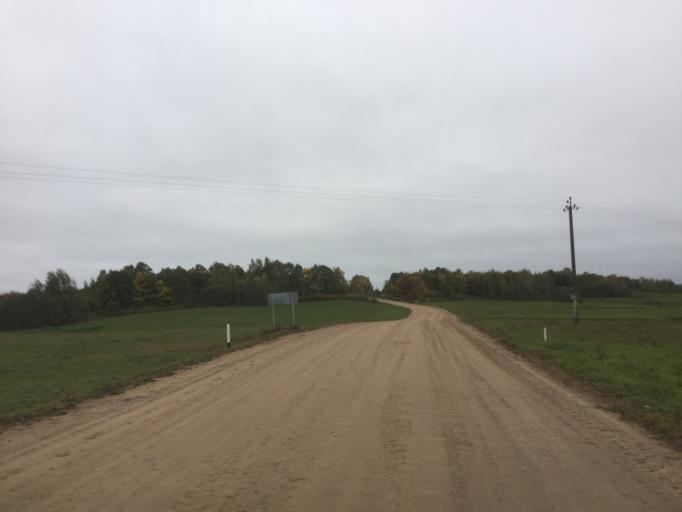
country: BY
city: Novolukoml'
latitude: 54.7163
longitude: 29.1400
